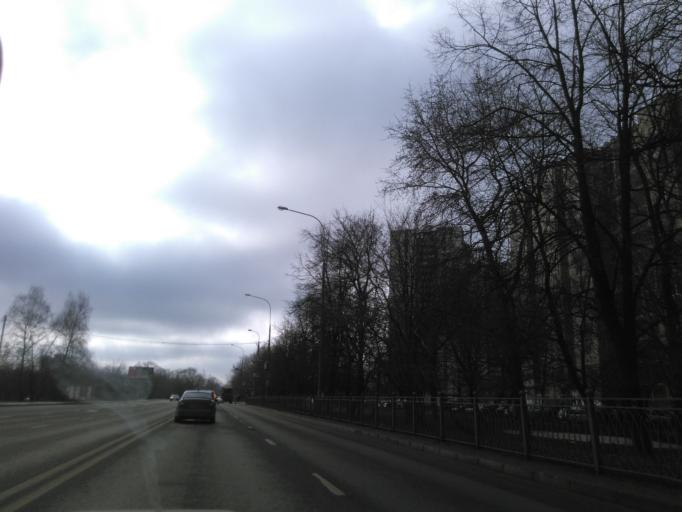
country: RU
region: Moscow
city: Khimki
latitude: 55.8698
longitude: 37.4437
